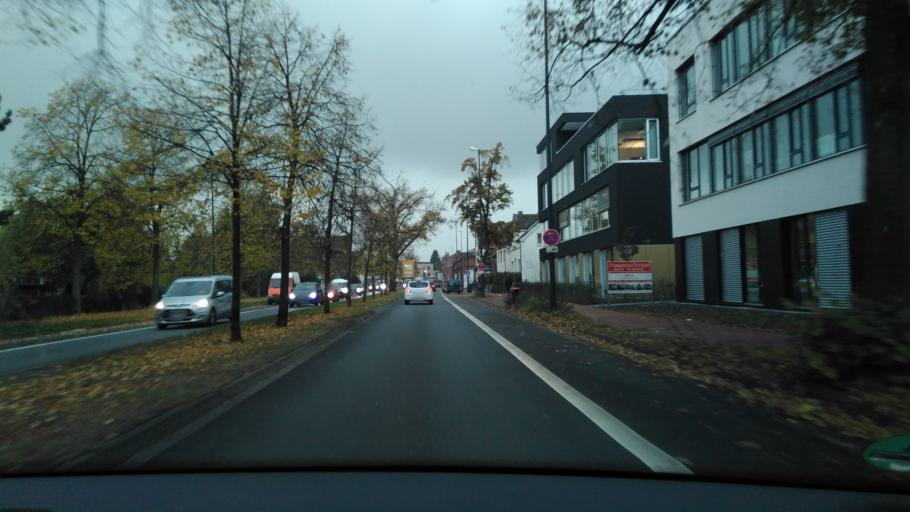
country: DE
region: North Rhine-Westphalia
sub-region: Regierungsbezirk Detmold
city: Guetersloh
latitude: 51.9025
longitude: 8.3960
